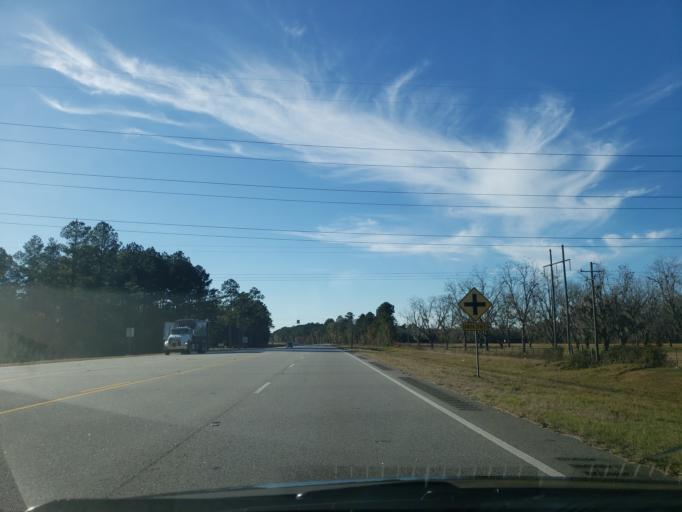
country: US
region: Georgia
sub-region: Ware County
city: Deenwood
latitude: 31.2094
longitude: -82.3992
